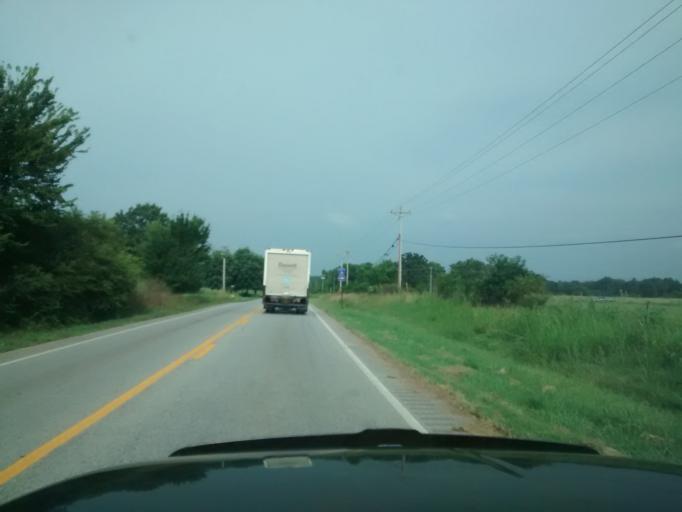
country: US
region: Arkansas
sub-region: Washington County
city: Farmington
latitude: 36.0759
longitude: -94.2827
